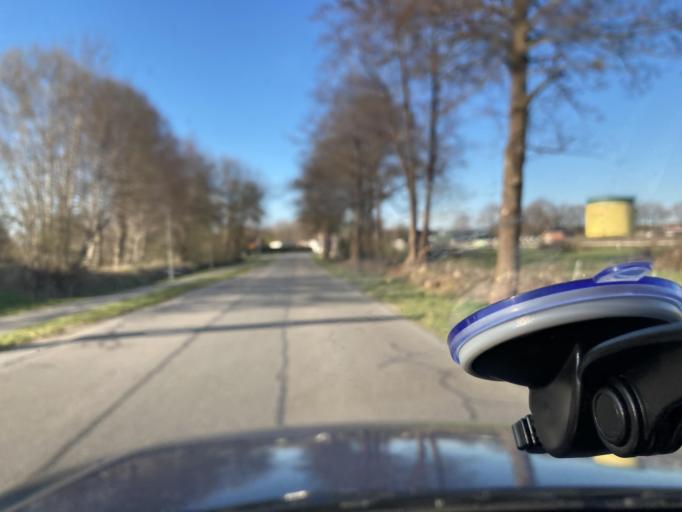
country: DE
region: Schleswig-Holstein
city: Heide
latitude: 54.2086
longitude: 9.0940
